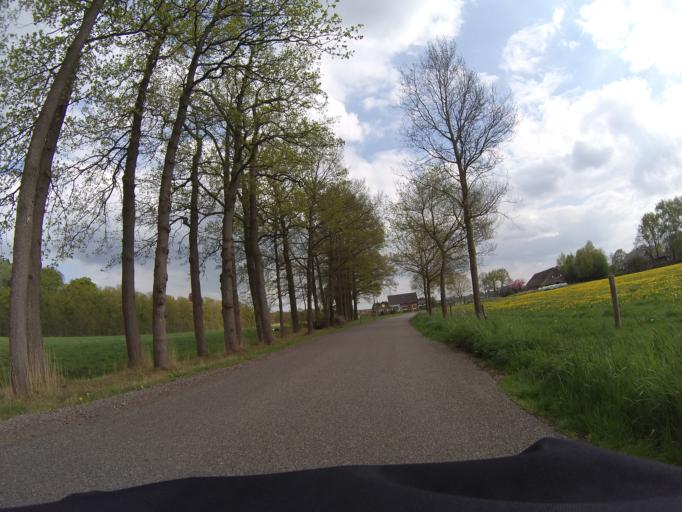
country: NL
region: Gelderland
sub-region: Gemeente Oldebroek
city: Oldebroek
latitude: 52.4606
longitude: 5.9526
